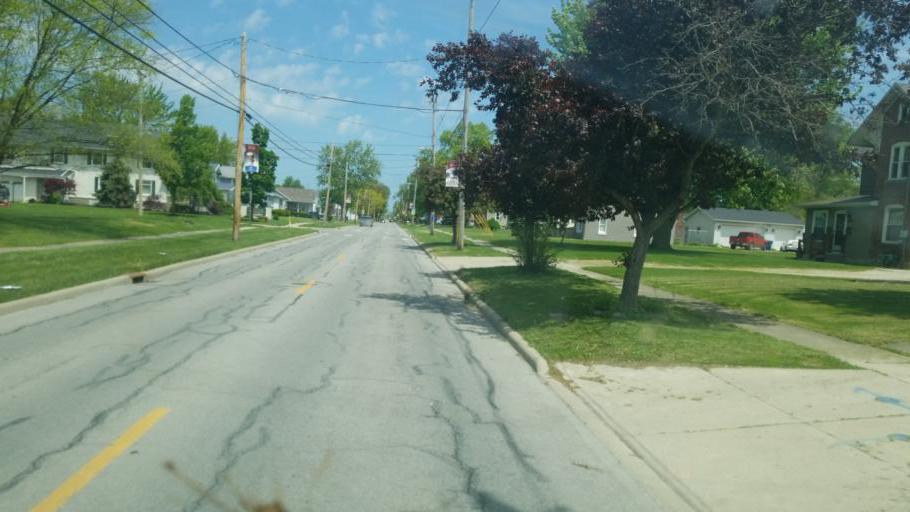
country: US
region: Ohio
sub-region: Ottawa County
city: Oak Harbor
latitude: 41.5116
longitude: -83.1450
